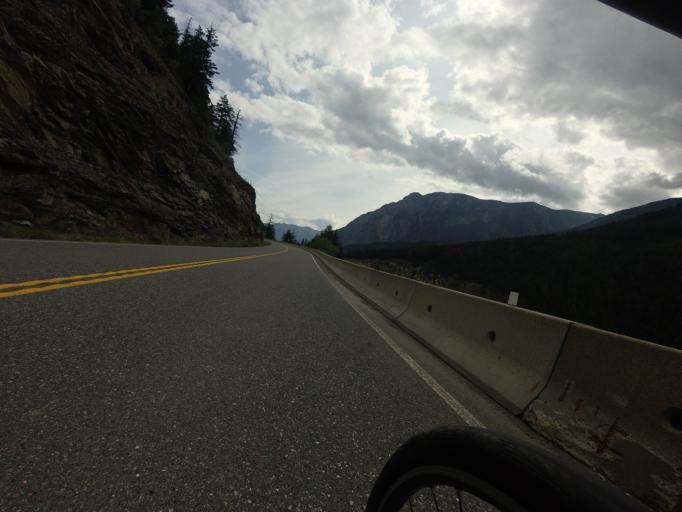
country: CA
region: British Columbia
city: Lillooet
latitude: 50.6421
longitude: -122.0251
